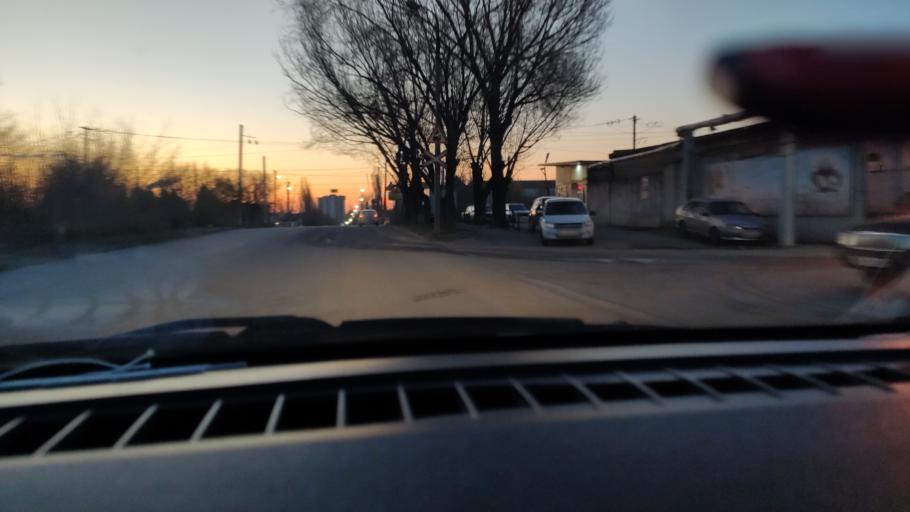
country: RU
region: Saratov
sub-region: Saratovskiy Rayon
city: Saratov
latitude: 51.6150
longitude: 45.9579
